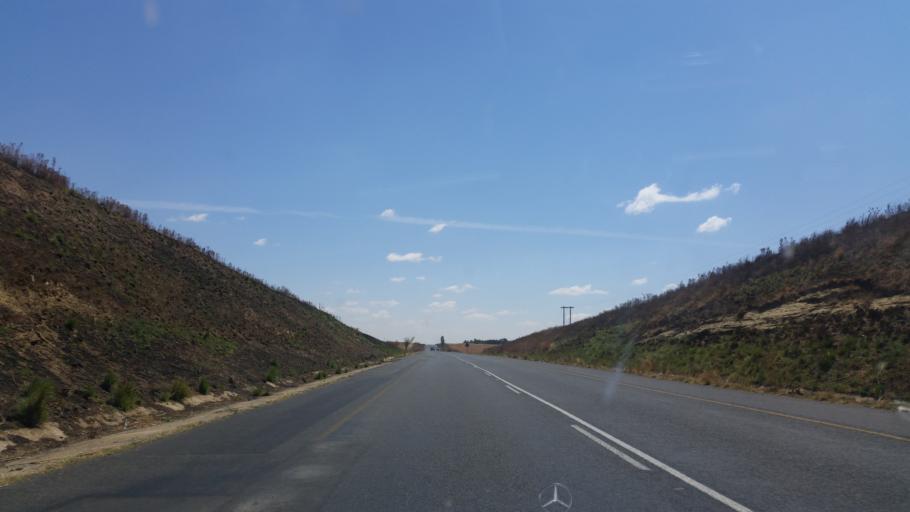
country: ZA
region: Orange Free State
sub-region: Thabo Mofutsanyana District Municipality
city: Bethlehem
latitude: -28.1136
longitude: 28.6750
